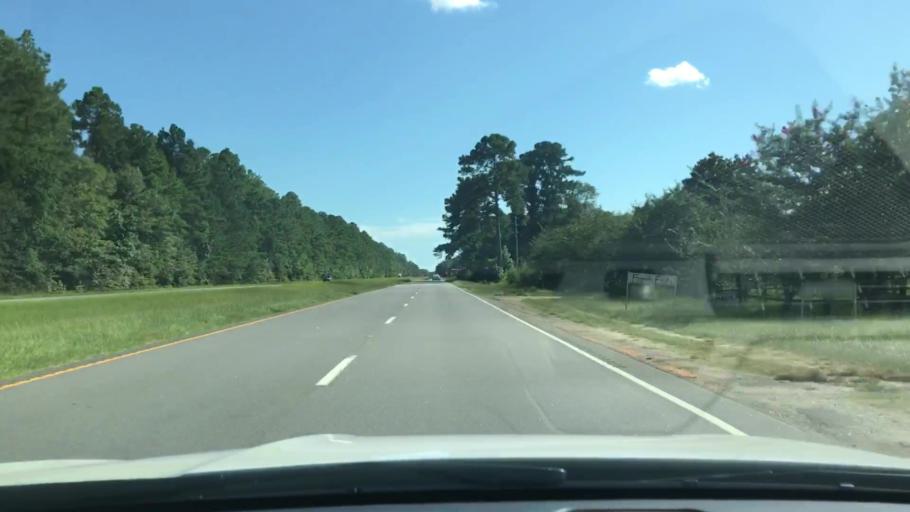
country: US
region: South Carolina
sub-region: Georgetown County
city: Georgetown
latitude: 33.2279
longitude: -79.3773
